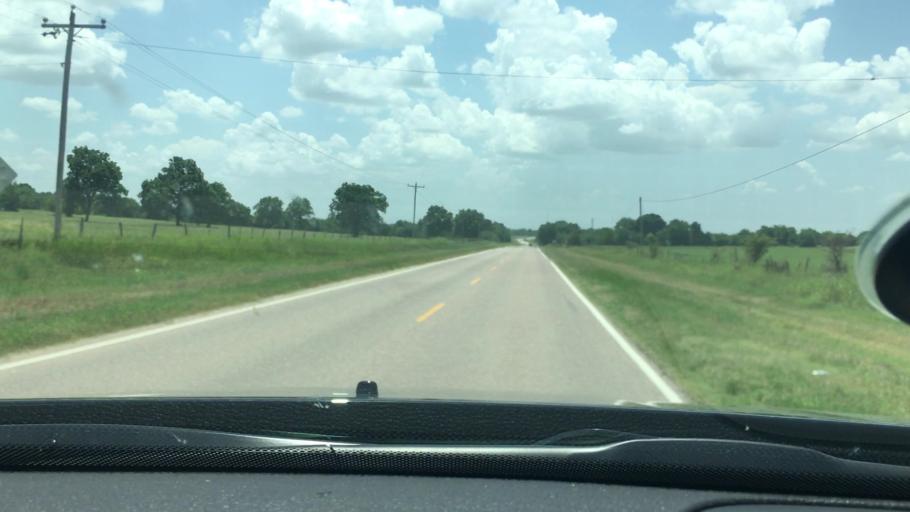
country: US
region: Oklahoma
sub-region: Johnston County
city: Tishomingo
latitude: 34.4682
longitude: -96.6360
